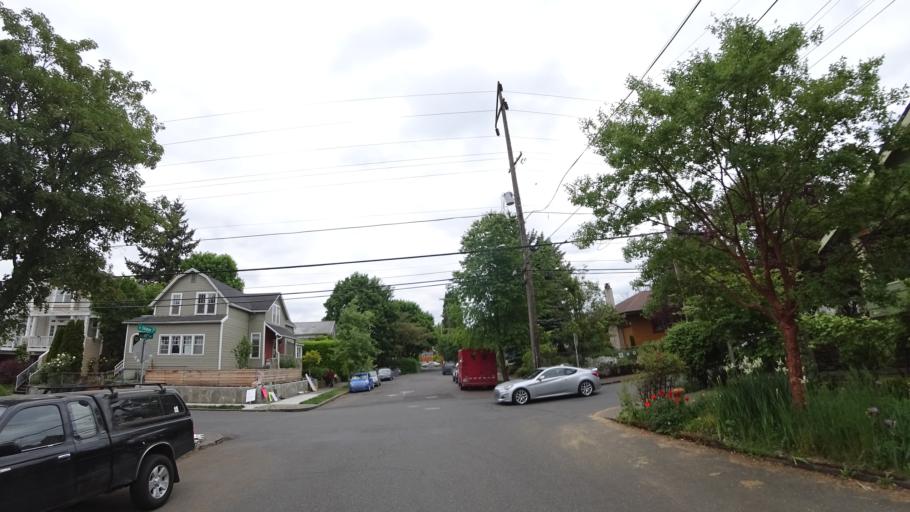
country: US
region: Oregon
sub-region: Multnomah County
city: Lents
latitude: 45.5143
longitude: -122.6164
